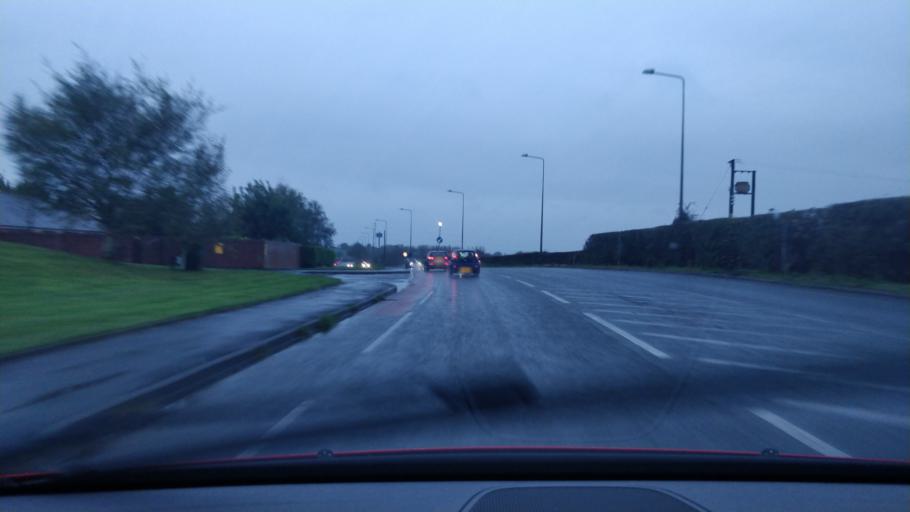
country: GB
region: England
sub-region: Lancashire
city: Poulton le Fylde
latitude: 53.7859
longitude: -2.9574
